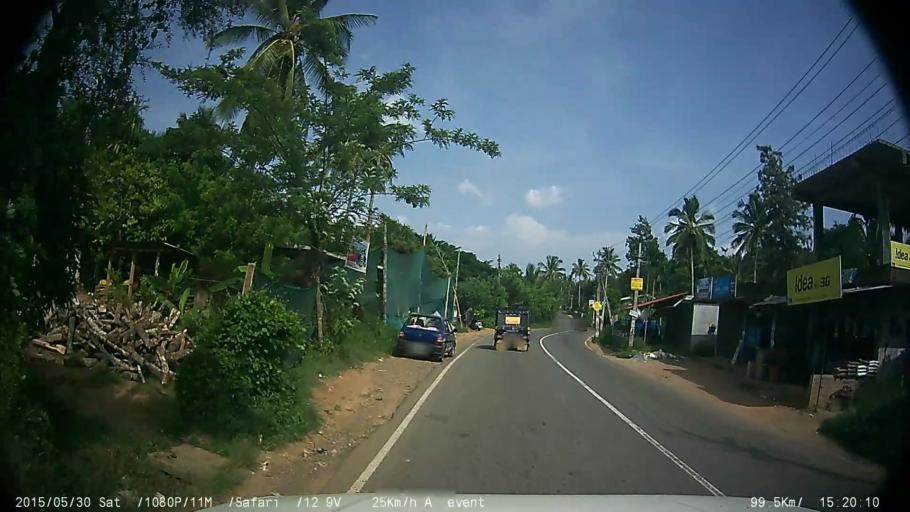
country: IN
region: Kerala
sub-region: Wayanad
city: Panamaram
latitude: 11.7551
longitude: 76.0643
